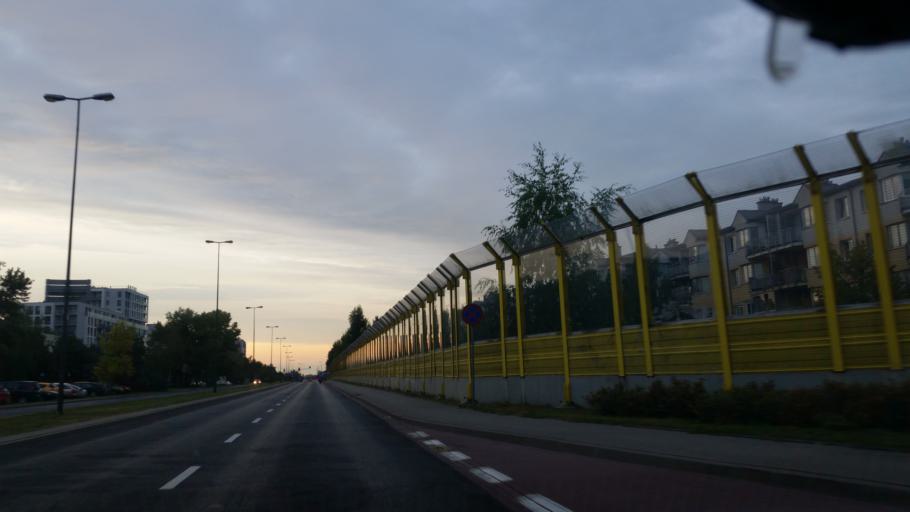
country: PL
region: Masovian Voivodeship
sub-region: Warszawa
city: Kabaty
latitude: 52.1398
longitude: 21.0687
